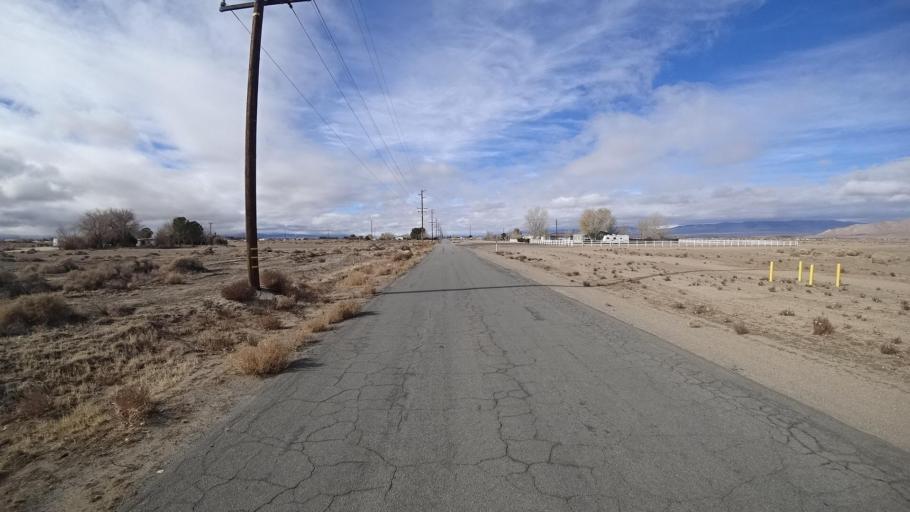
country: US
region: California
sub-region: Kern County
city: Rosamond
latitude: 34.8346
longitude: -118.2490
